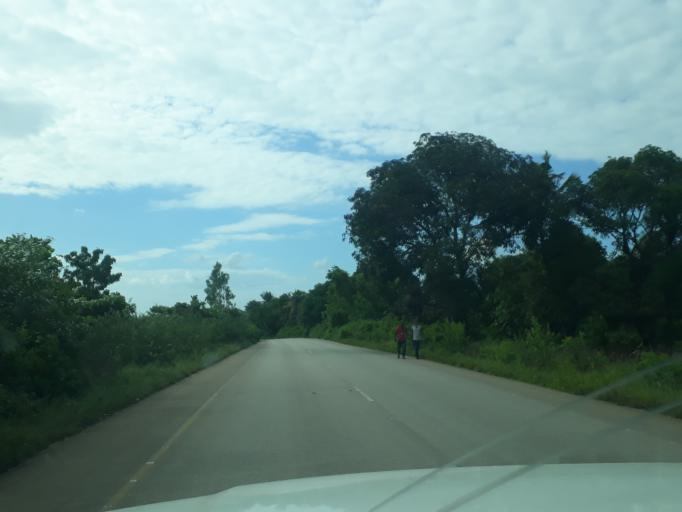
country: TZ
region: Zanzibar North
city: Kijini
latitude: -5.8468
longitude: 39.2837
